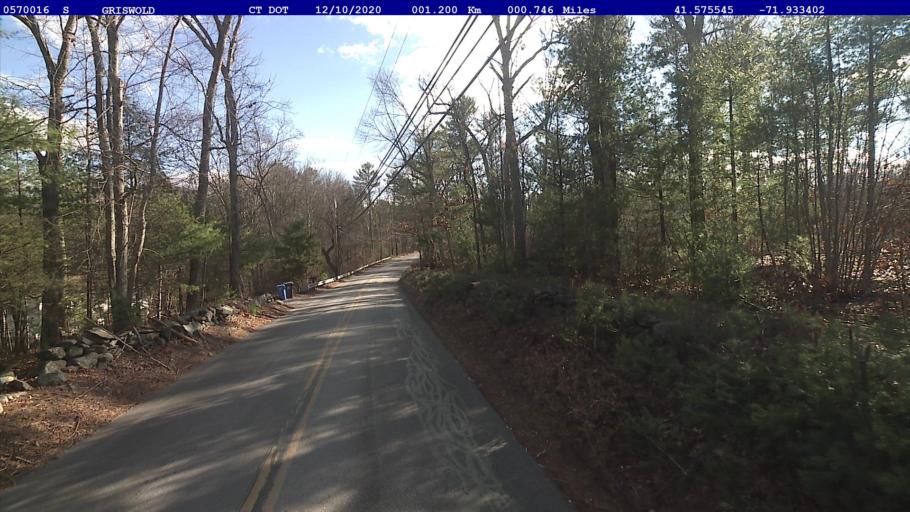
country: US
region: Connecticut
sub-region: New London County
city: Jewett City
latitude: 41.5755
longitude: -71.9334
